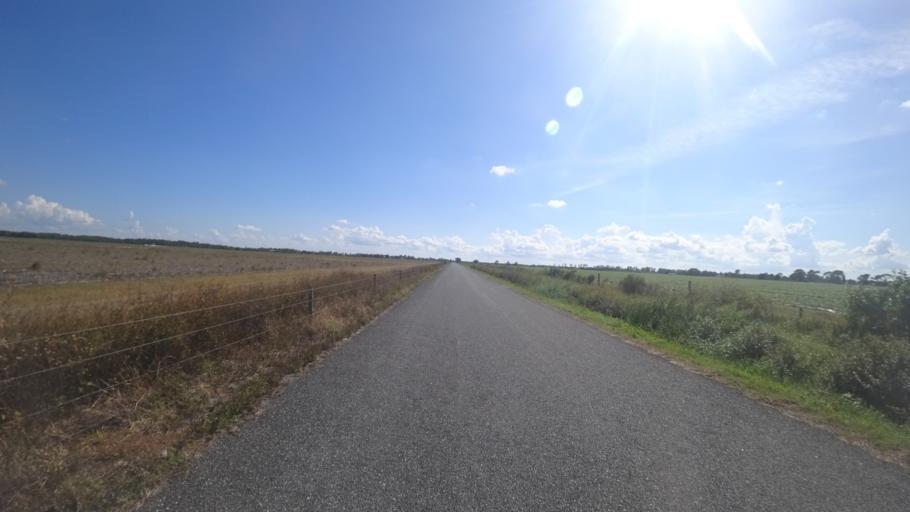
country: US
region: Florida
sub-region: Sarasota County
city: The Meadows
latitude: 27.4393
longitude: -82.2871
